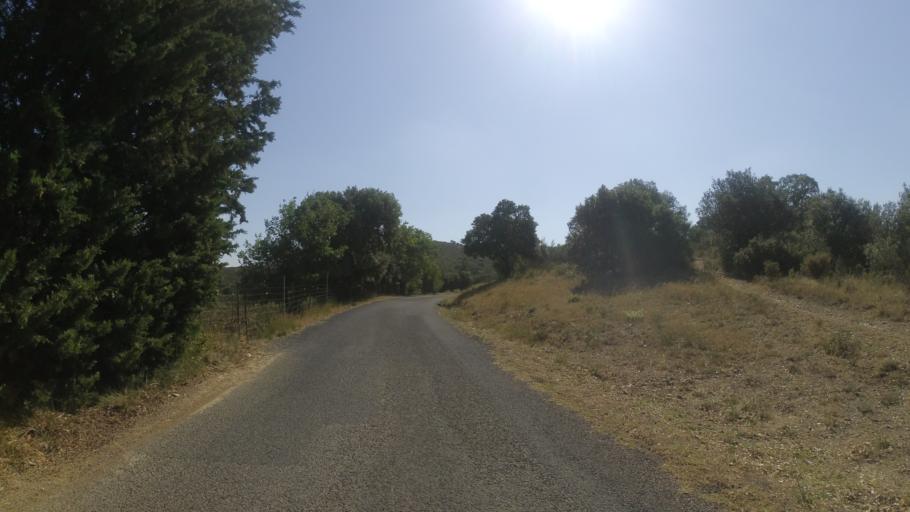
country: FR
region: Languedoc-Roussillon
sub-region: Departement des Pyrenees-Orientales
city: Thuir
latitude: 42.6148
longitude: 2.6844
